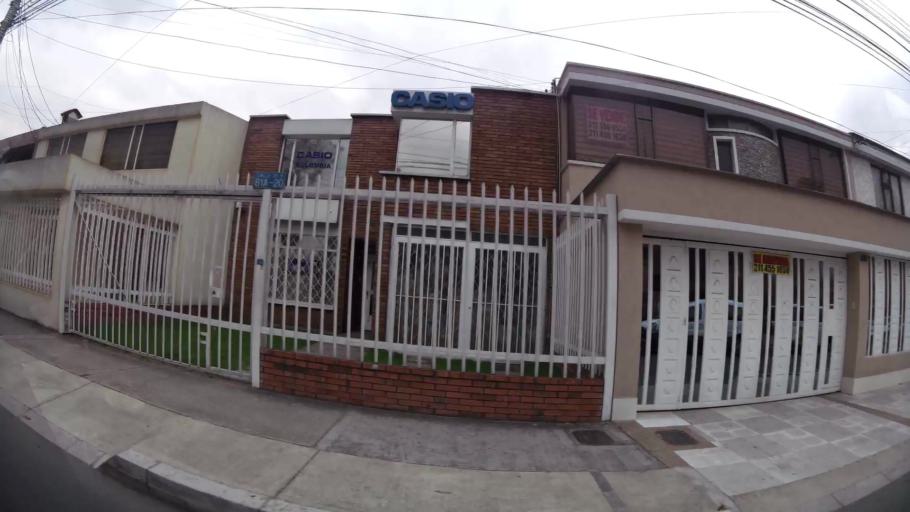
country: CO
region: Bogota D.C.
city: Bogota
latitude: 4.6704
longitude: -74.1194
